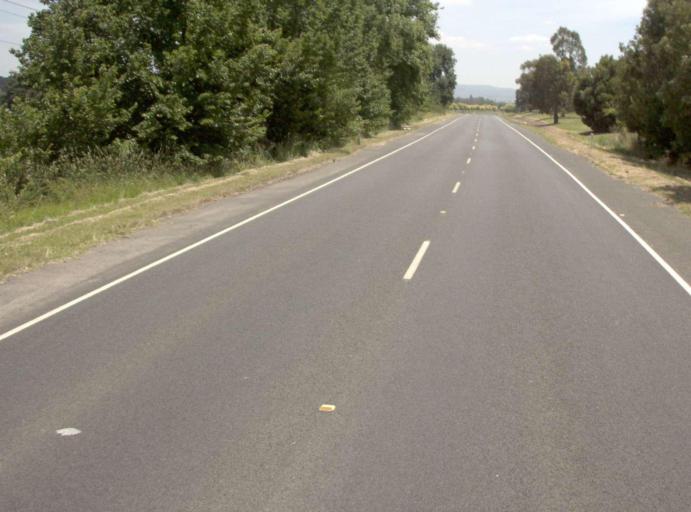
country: AU
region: Victoria
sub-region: Latrobe
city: Traralgon
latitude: -38.2135
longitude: 146.5462
